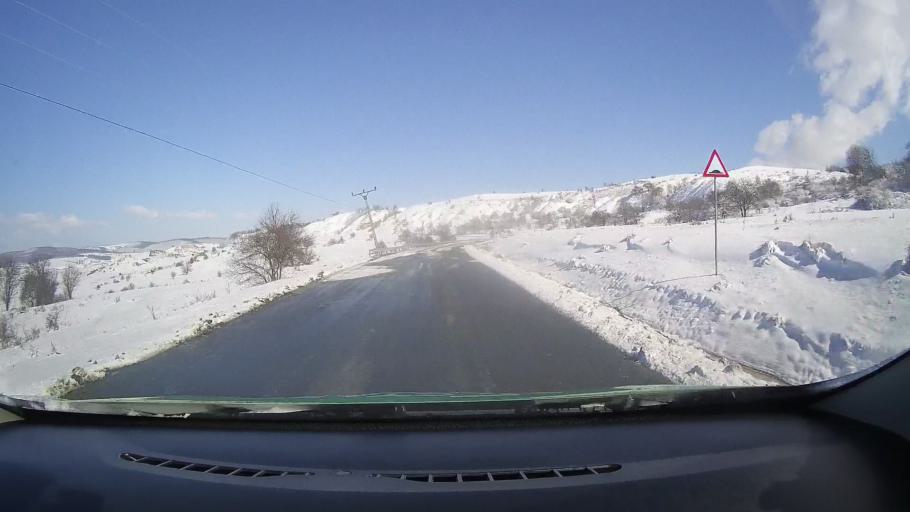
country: RO
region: Sibiu
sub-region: Comuna Avrig
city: Avrig
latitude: 45.7794
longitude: 24.3711
